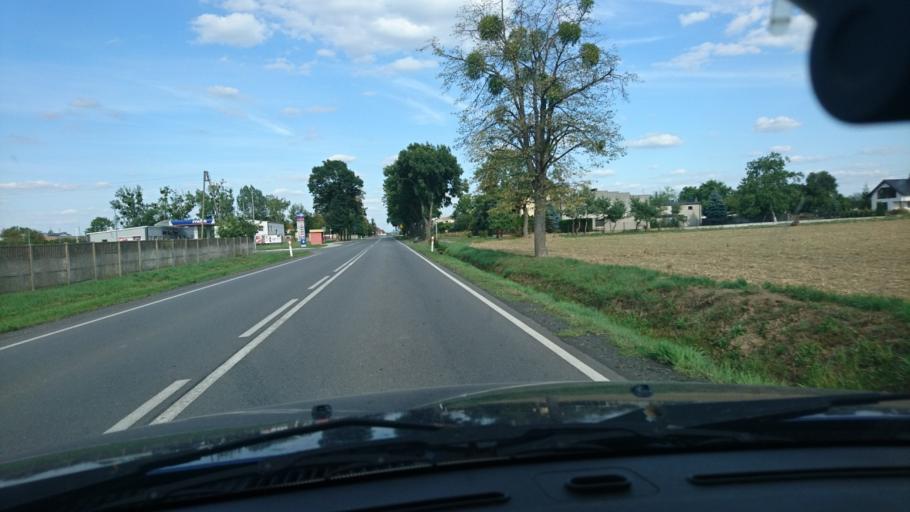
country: PL
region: Greater Poland Voivodeship
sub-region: Powiat krotoszynski
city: Kobylin
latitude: 51.7317
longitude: 17.3098
